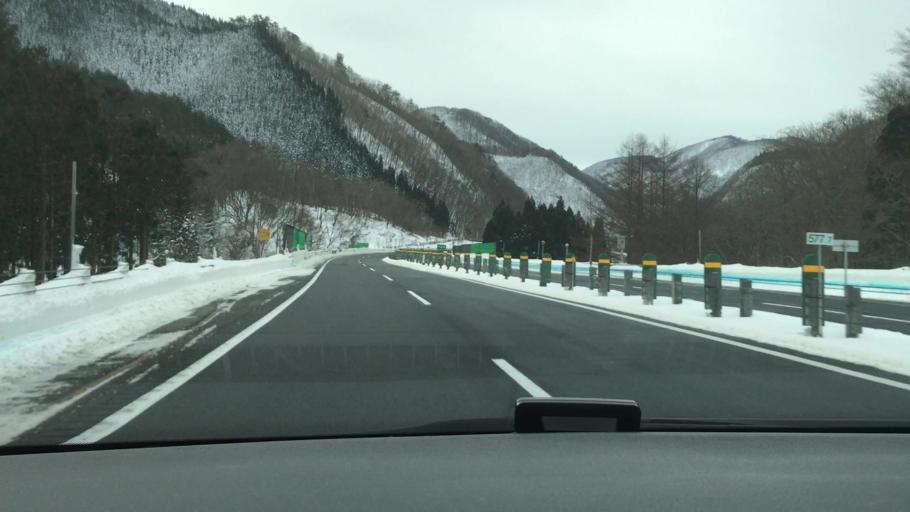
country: JP
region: Akita
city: Hanawa
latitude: 40.1285
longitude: 140.9120
